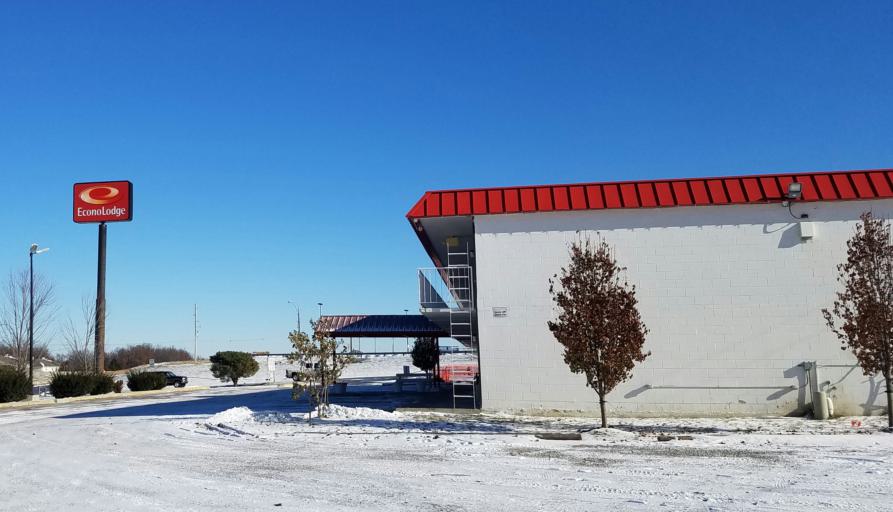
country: US
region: Missouri
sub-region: Jackson County
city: Oak Grove
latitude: 39.0151
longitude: -94.1257
